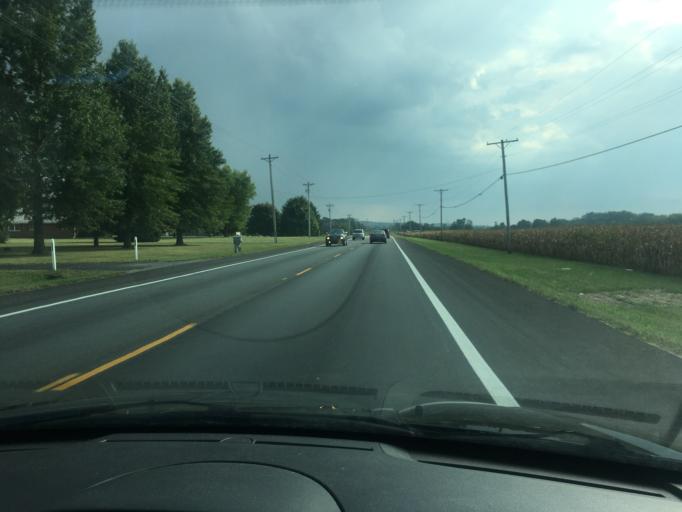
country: US
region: Ohio
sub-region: Champaign County
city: Urbana
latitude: 40.0533
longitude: -83.7786
